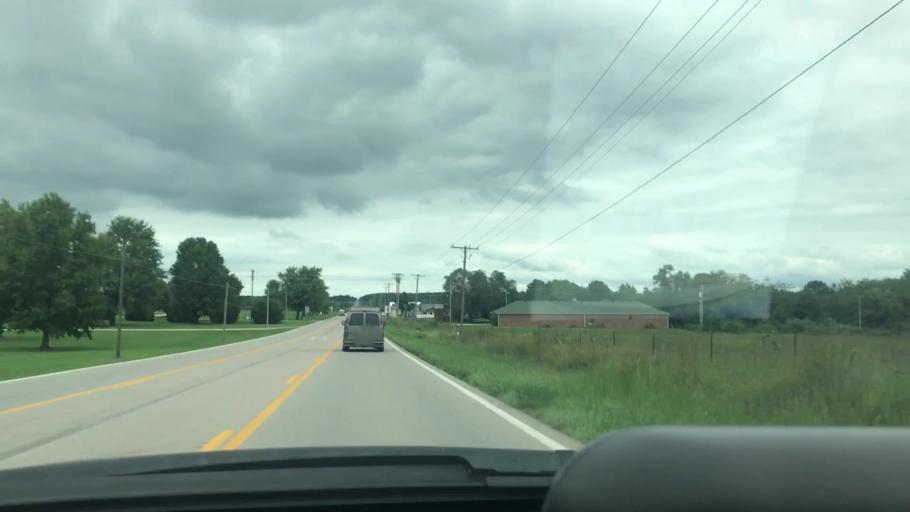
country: US
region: Missouri
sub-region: Dallas County
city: Buffalo
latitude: 37.6532
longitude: -93.1038
